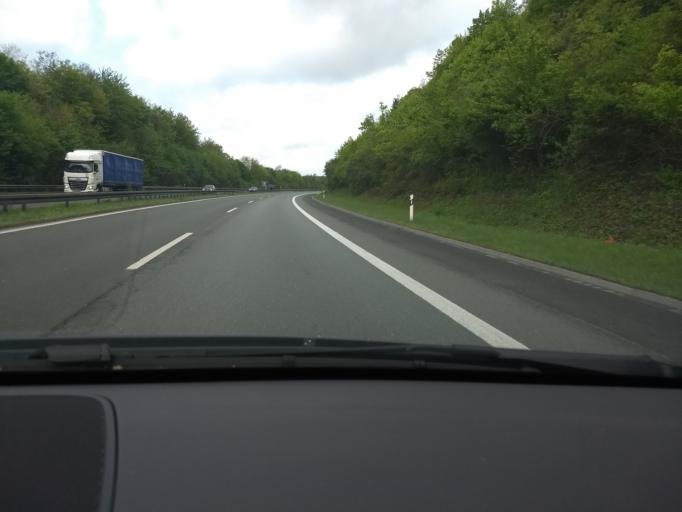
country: DE
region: North Rhine-Westphalia
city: Wickede
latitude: 51.4737
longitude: 7.9341
